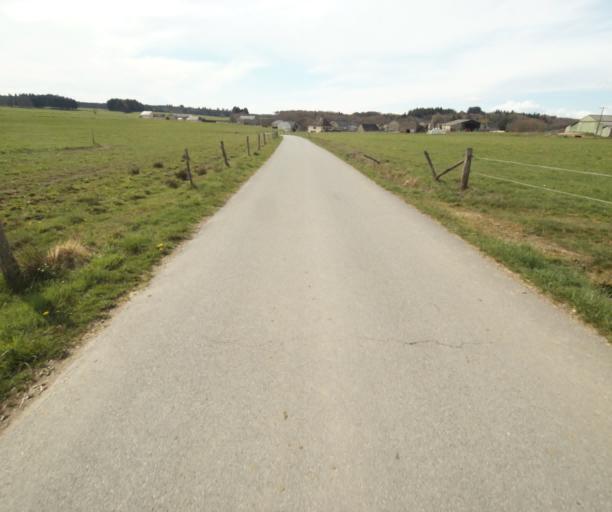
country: FR
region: Limousin
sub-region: Departement de la Correze
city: Correze
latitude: 45.3565
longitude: 1.8857
